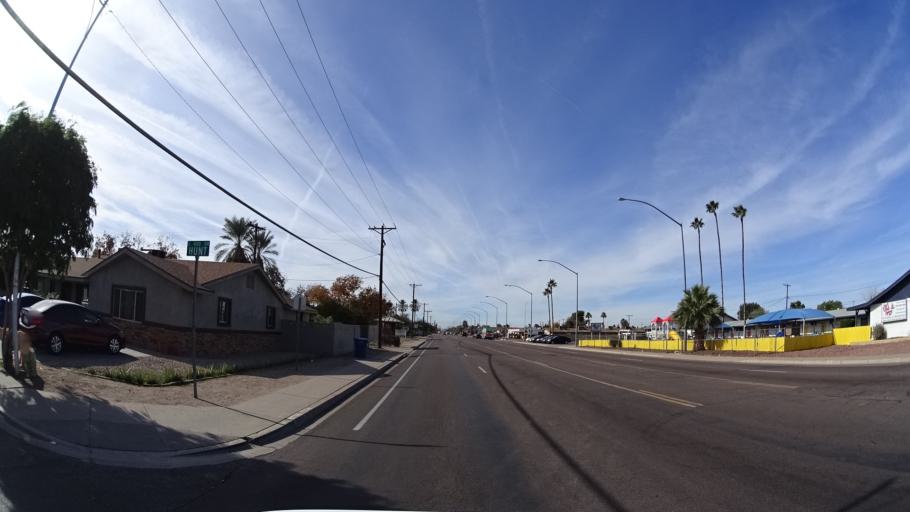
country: US
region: Arizona
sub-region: Maricopa County
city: Mesa
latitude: 33.4080
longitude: -111.7987
